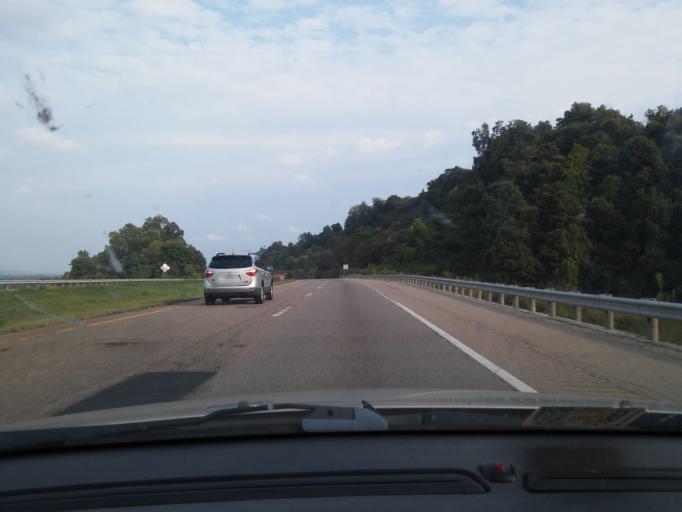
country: US
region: West Virginia
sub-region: Mason County
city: Point Pleasant
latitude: 38.8236
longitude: -82.1263
